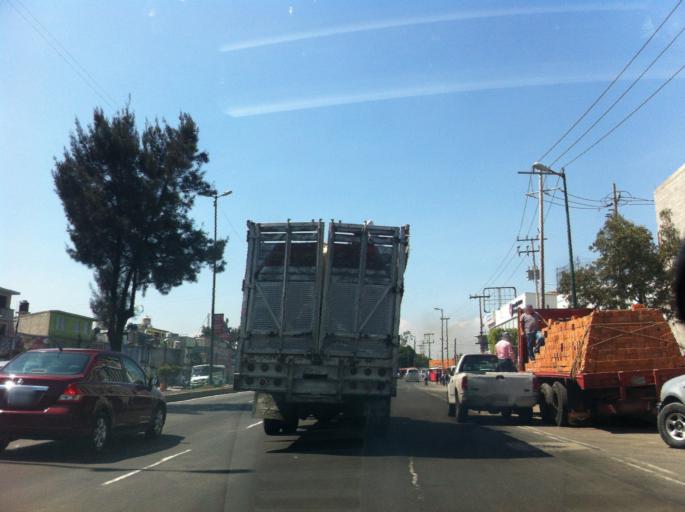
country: MX
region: Mexico
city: Los Reyes La Paz
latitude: 19.3555
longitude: -99.0079
